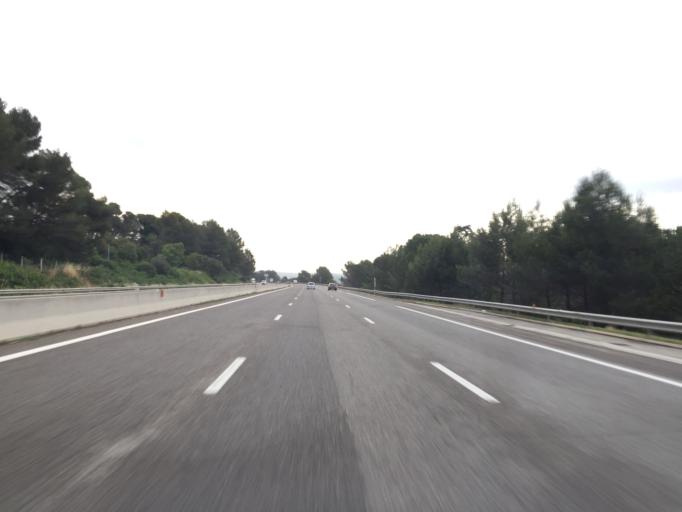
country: FR
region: Provence-Alpes-Cote d'Azur
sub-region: Departement du Var
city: La Celle
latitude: 43.4184
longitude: 6.0431
